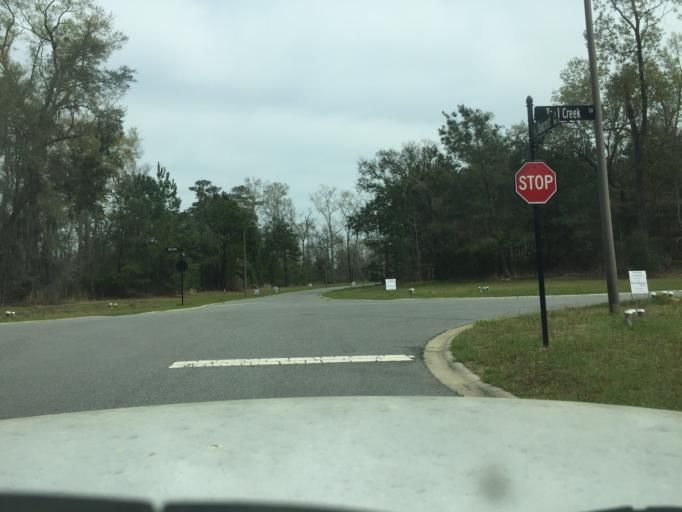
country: US
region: Georgia
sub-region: Chatham County
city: Pooler
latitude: 32.0518
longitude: -81.2447
